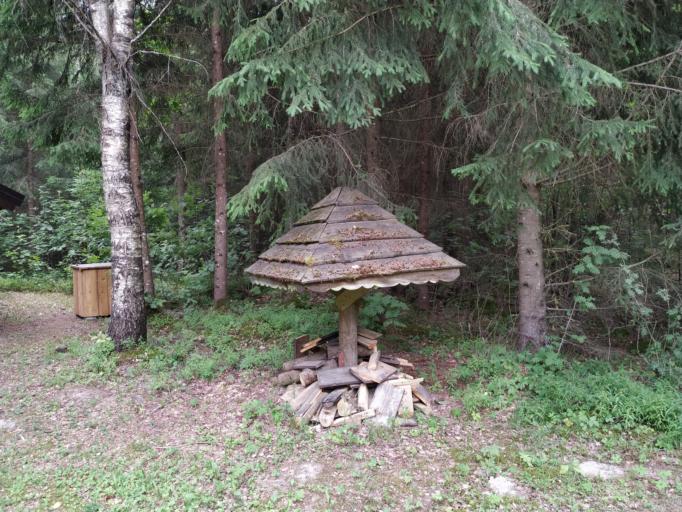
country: LT
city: Obeliai
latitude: 56.1564
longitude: 25.1072
